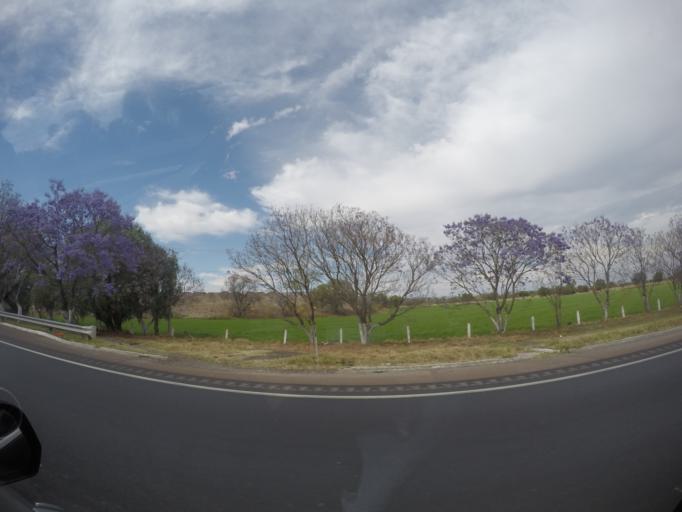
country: MX
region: Guanajuato
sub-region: Apaseo el Grande
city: La Labor
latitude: 20.5354
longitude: -100.7119
